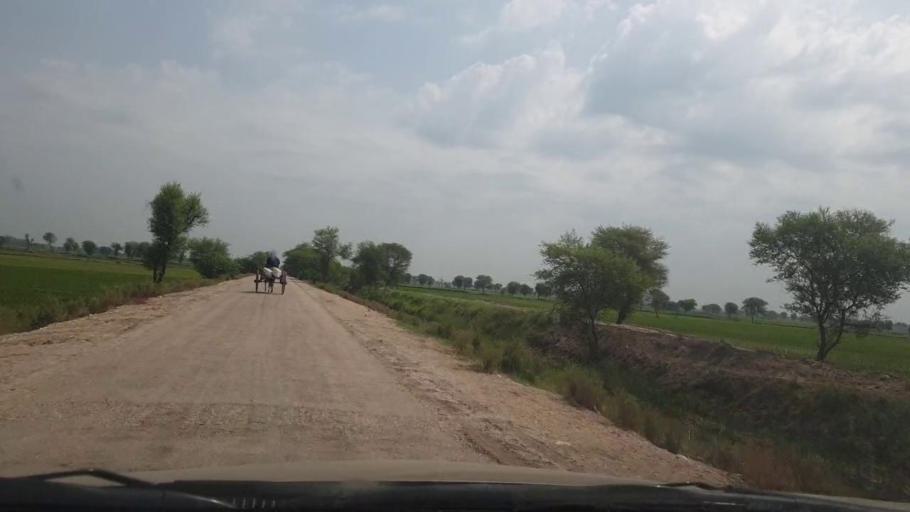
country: PK
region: Sindh
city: Miro Khan
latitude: 27.6837
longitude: 68.1886
